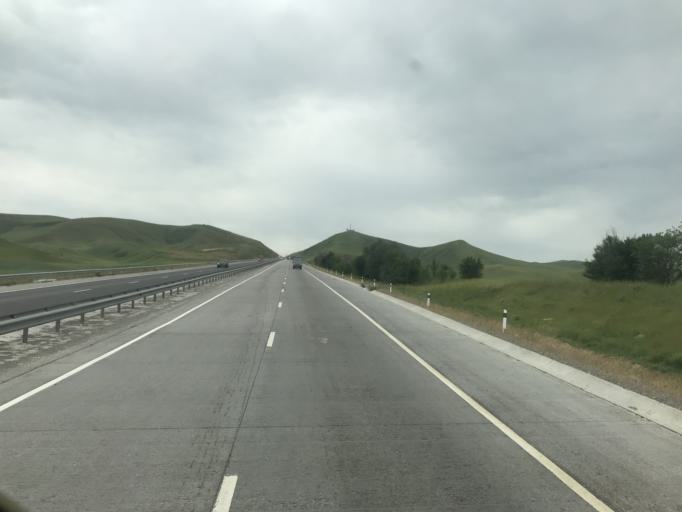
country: KZ
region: Ongtustik Qazaqstan
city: Qazyqurt
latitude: 42.0181
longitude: 69.4701
